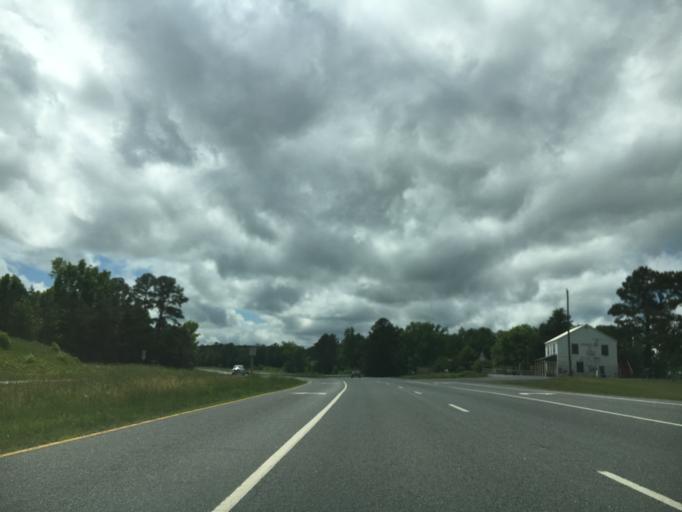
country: US
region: Virginia
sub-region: Mecklenburg County
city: Clarksville
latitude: 36.6511
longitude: -78.4915
